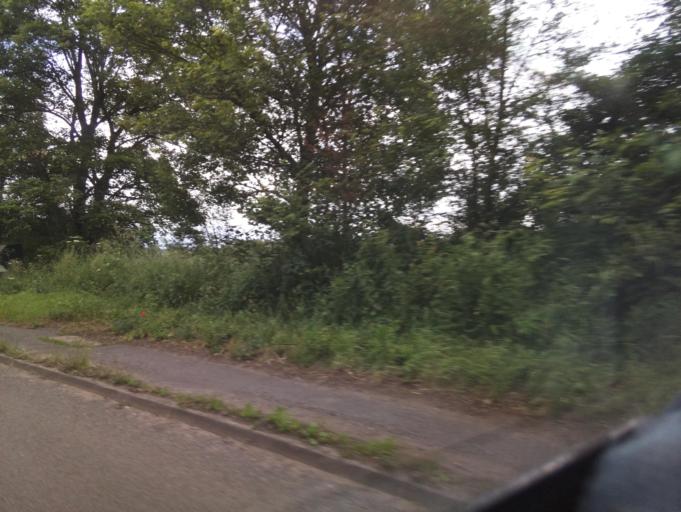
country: GB
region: England
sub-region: Dudley
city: Kingswinford
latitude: 52.4700
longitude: -2.1957
